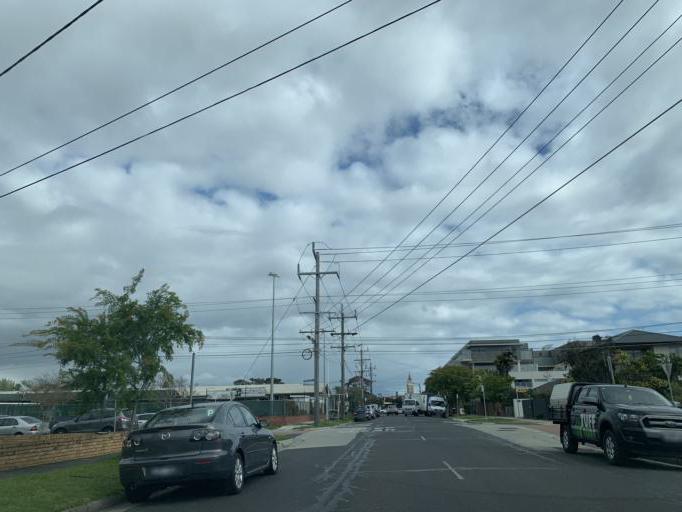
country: AU
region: Victoria
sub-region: Kingston
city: Mentone
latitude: -37.9799
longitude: 145.0659
